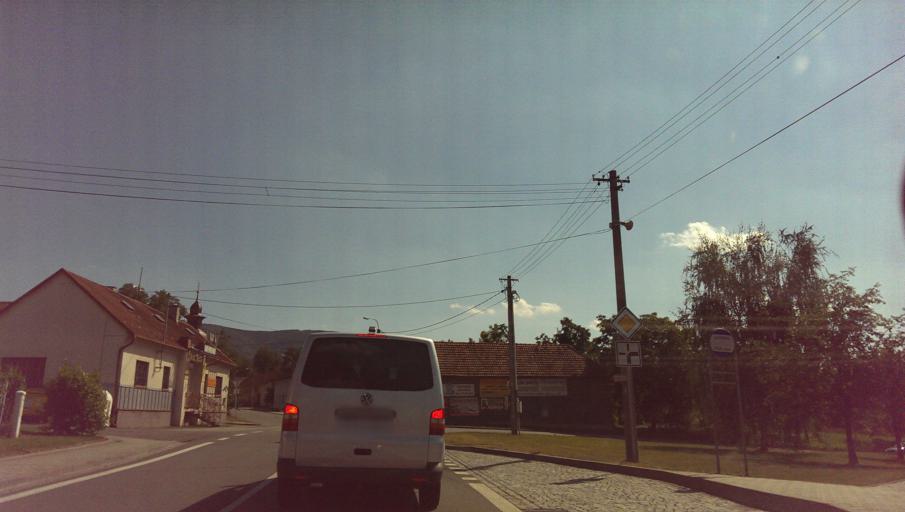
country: CZ
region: Zlin
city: Chvalcov
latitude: 49.4304
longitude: 17.7513
